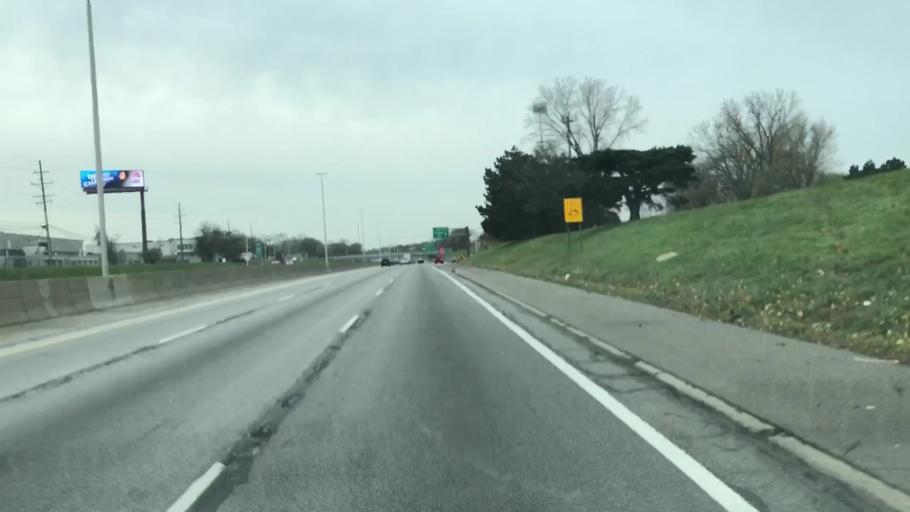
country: US
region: Michigan
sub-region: Wayne County
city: Grosse Pointe Woods
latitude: 42.4701
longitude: -82.9184
